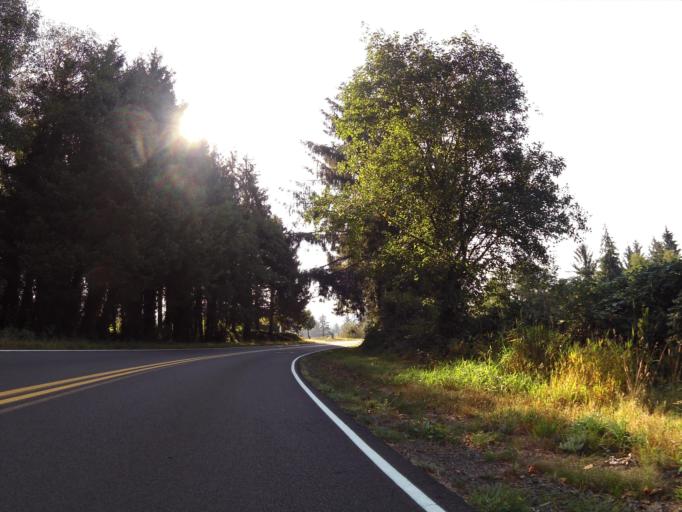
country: US
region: Oregon
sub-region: Tillamook County
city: Tillamook
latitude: 45.4012
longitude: -123.7935
